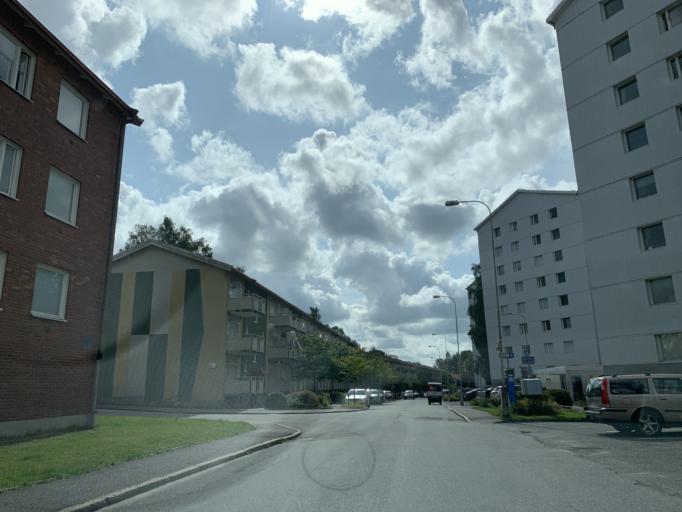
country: SE
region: Vaestra Goetaland
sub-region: Goteborg
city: Eriksbo
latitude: 57.7610
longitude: 12.0331
